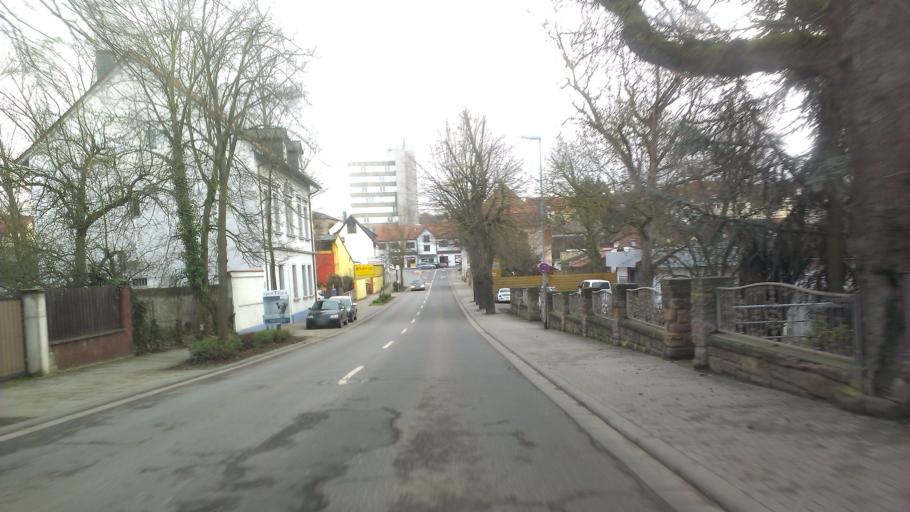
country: DE
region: Rheinland-Pfalz
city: Alzey
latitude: 49.7449
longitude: 8.1057
